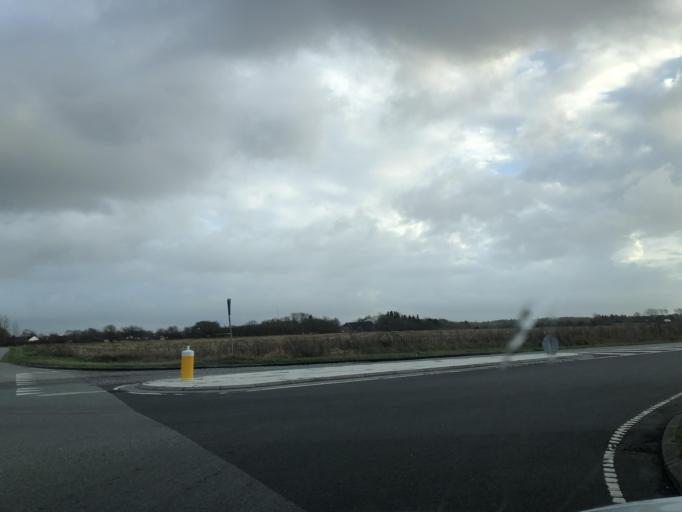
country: DK
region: South Denmark
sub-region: Esbjerg Kommune
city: Bramming
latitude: 55.4034
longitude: 8.7289
